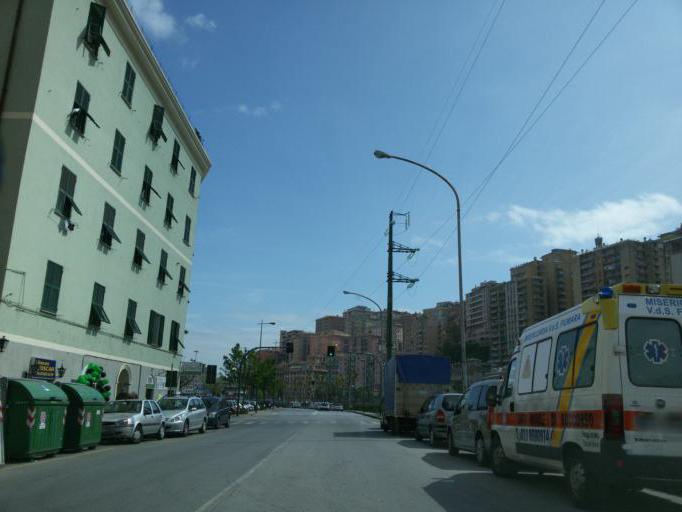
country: IT
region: Liguria
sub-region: Provincia di Genova
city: Genoa
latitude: 44.4195
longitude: 8.9493
